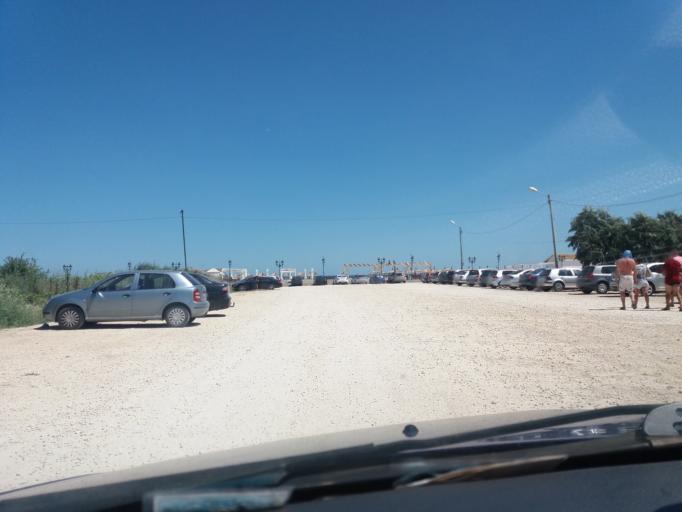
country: RO
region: Constanta
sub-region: Comuna Navodari
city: Navodari
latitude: 44.3198
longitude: 28.6341
